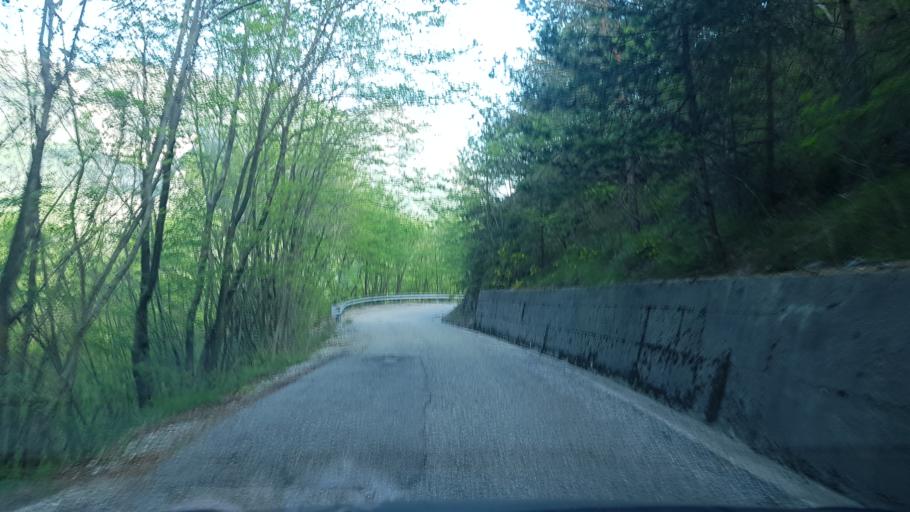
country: IT
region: Friuli Venezia Giulia
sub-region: Provincia di Udine
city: Trasaghis
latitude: 46.3146
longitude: 13.0412
